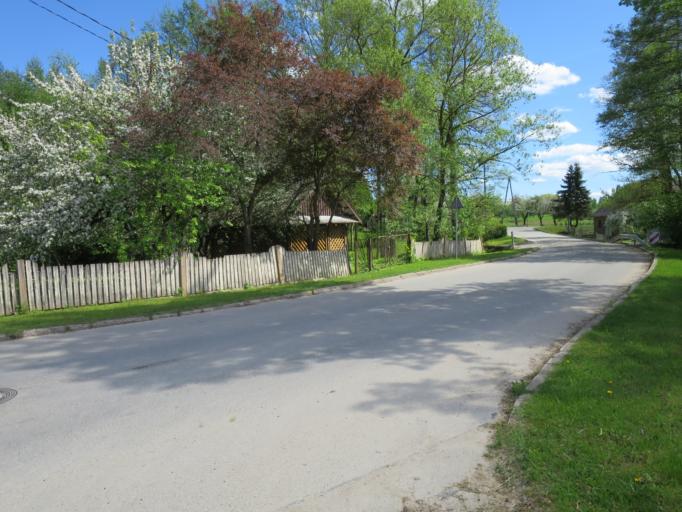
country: LV
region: Baldone
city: Baldone
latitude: 56.7401
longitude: 24.3955
